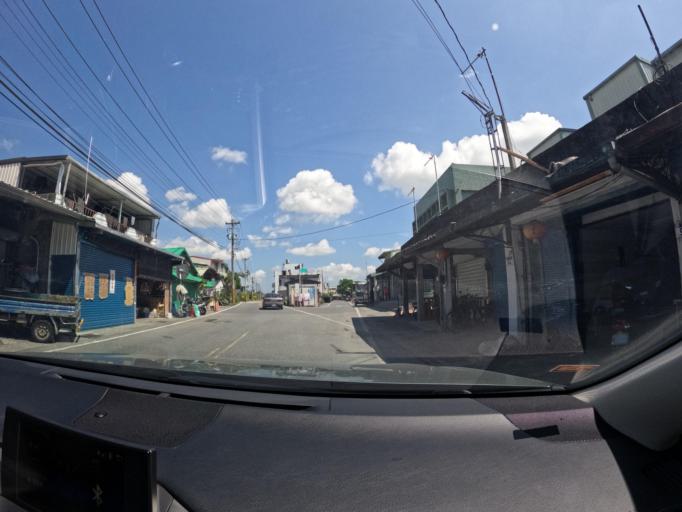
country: TW
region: Taiwan
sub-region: Hualien
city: Hualian
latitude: 23.5789
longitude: 121.3779
